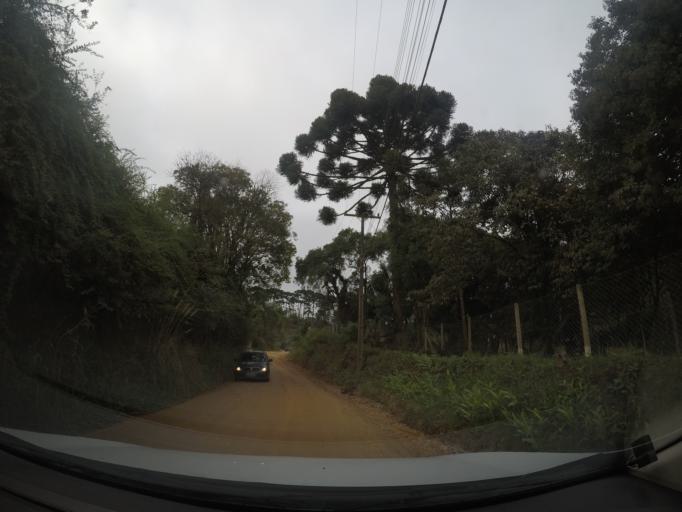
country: BR
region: Parana
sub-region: Colombo
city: Colombo
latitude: -25.3223
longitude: -49.2531
